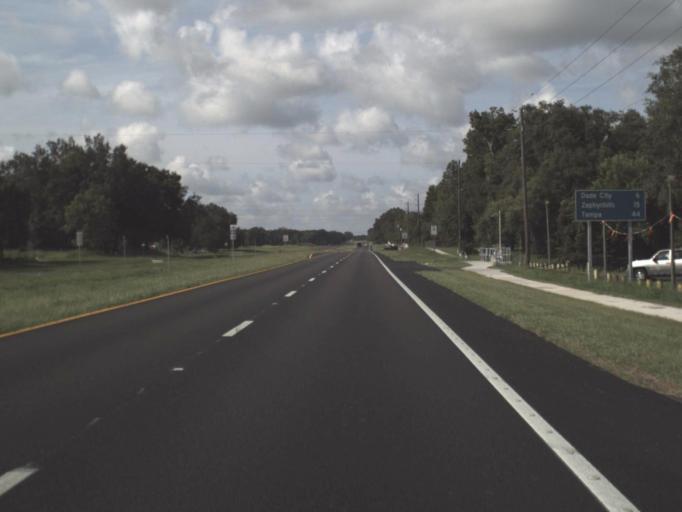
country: US
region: Florida
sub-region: Pasco County
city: Lacoochee
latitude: 28.4520
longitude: -82.1869
